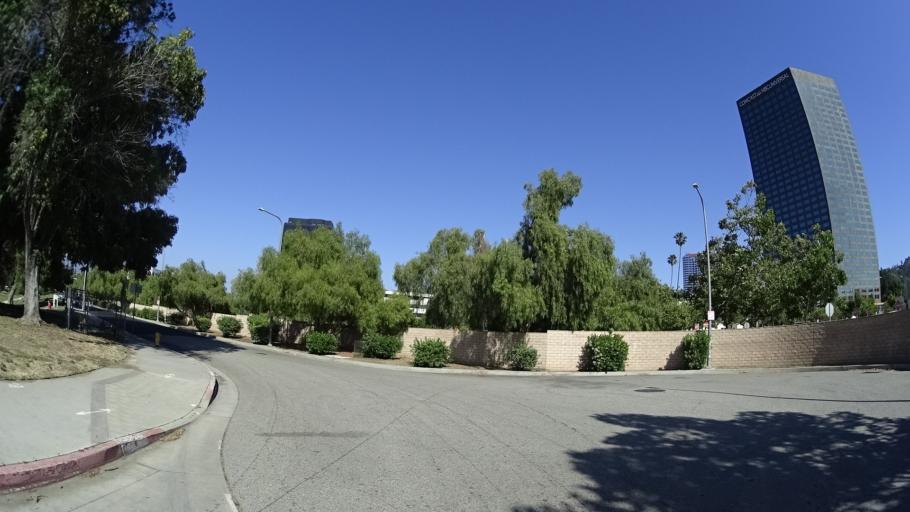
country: US
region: California
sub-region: Los Angeles County
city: Universal City
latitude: 34.1405
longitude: -118.3631
